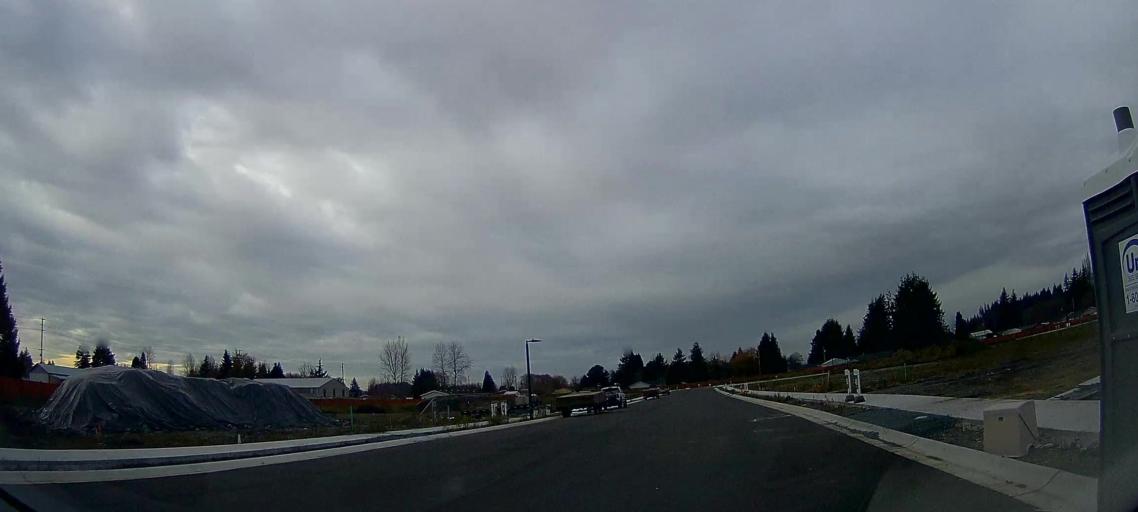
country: US
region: Washington
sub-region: Skagit County
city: Sedro-Woolley
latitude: 48.5164
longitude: -122.2440
